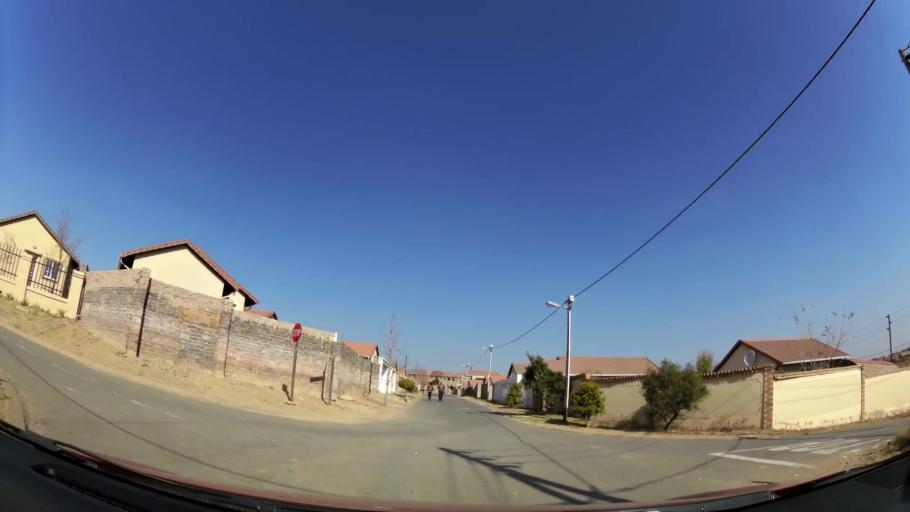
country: ZA
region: Gauteng
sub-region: West Rand District Municipality
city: Muldersdriseloop
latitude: -26.0333
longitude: 27.9207
